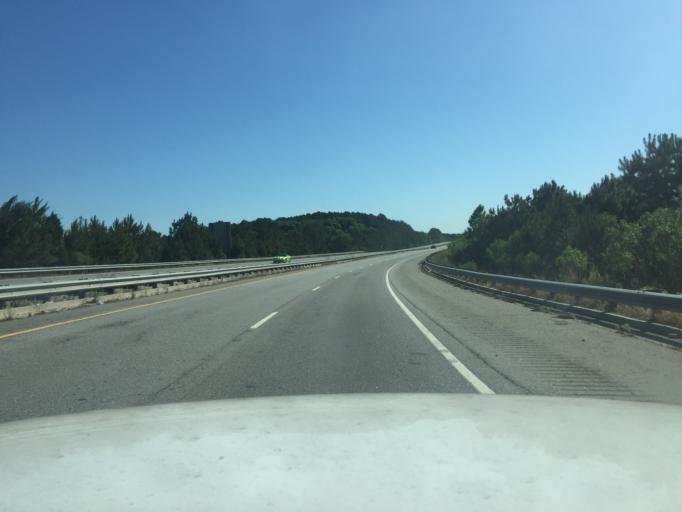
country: US
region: Georgia
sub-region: Chatham County
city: Georgetown
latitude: 32.0029
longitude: -81.1992
